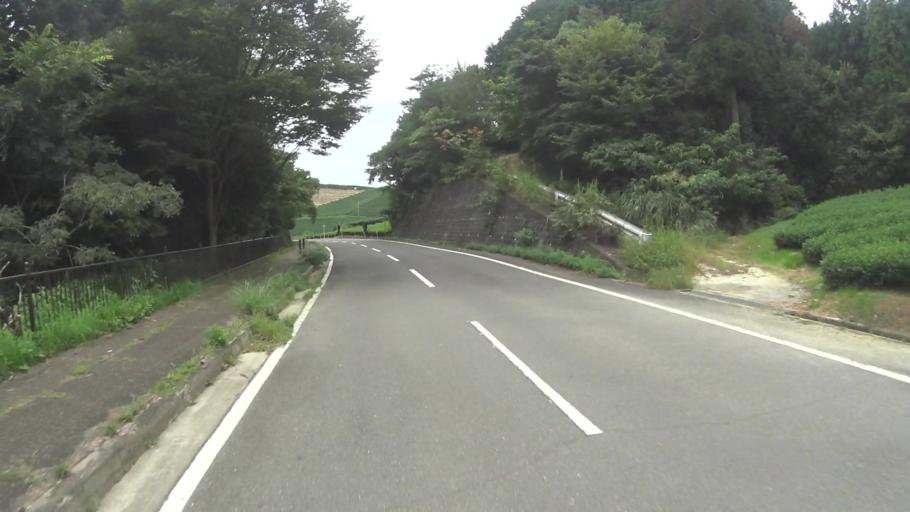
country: JP
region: Kyoto
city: Uji
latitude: 34.8058
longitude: 135.8951
